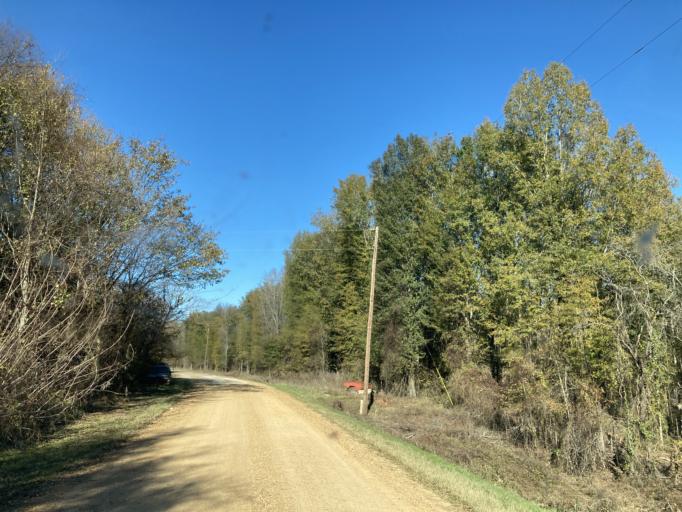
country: US
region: Mississippi
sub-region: Sharkey County
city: Rolling Fork
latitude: 32.7587
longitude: -90.6884
